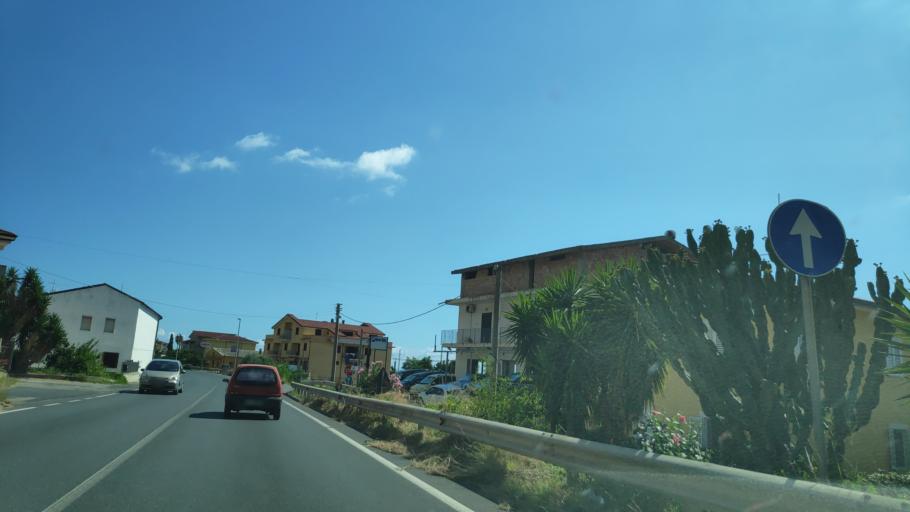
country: IT
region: Calabria
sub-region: Provincia di Cosenza
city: Campora San Giovanni
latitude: 39.0912
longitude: 16.0853
